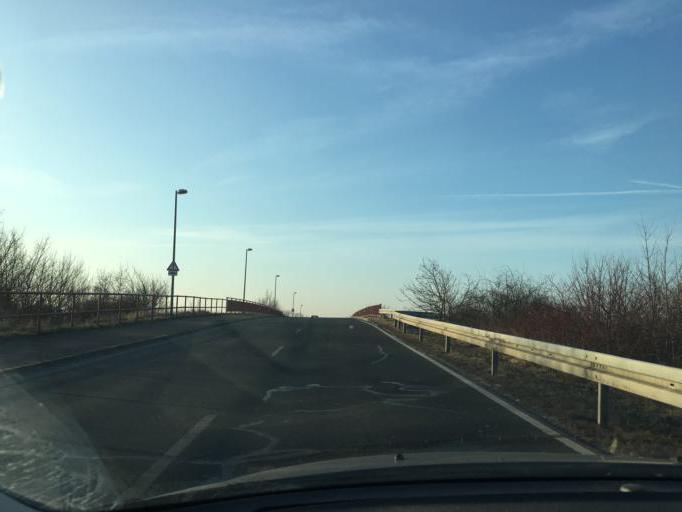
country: DE
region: Saxony
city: Borsdorf
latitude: 51.3442
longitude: 12.5194
